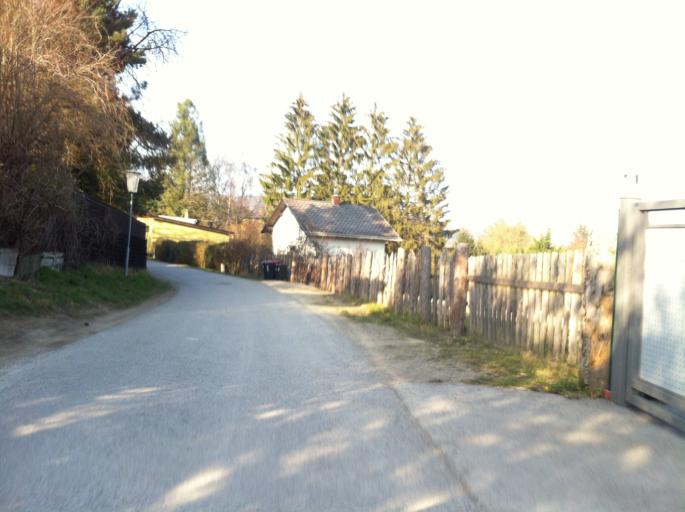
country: AT
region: Lower Austria
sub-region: Politischer Bezirk Wien-Umgebung
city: Wolfsgraben
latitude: 48.1790
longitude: 16.1080
